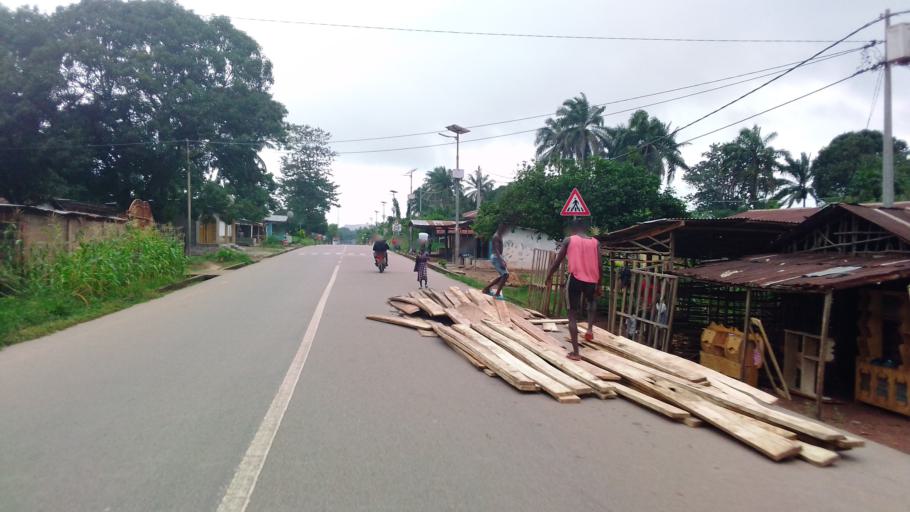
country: SL
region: Northern Province
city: Lunsar
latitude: 8.6872
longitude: -12.5410
